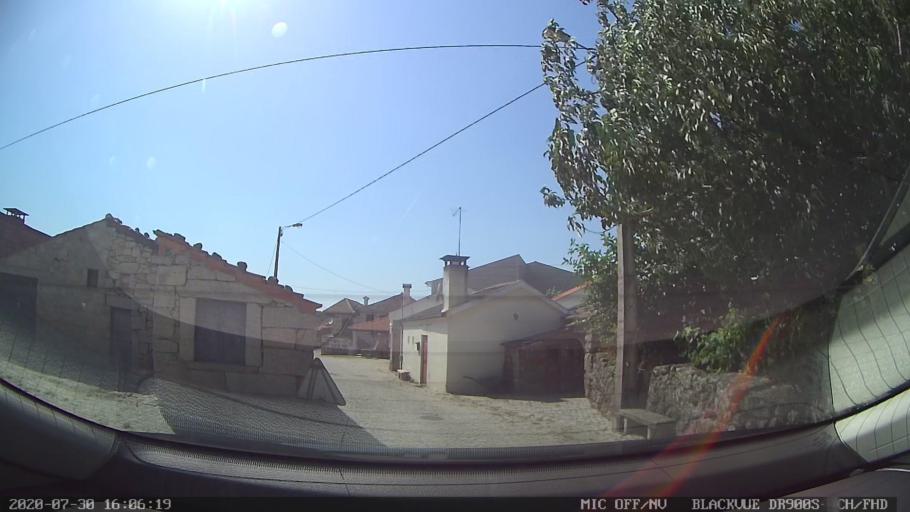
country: PT
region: Vila Real
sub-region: Murca
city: Murca
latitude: 41.3468
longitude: -7.4825
